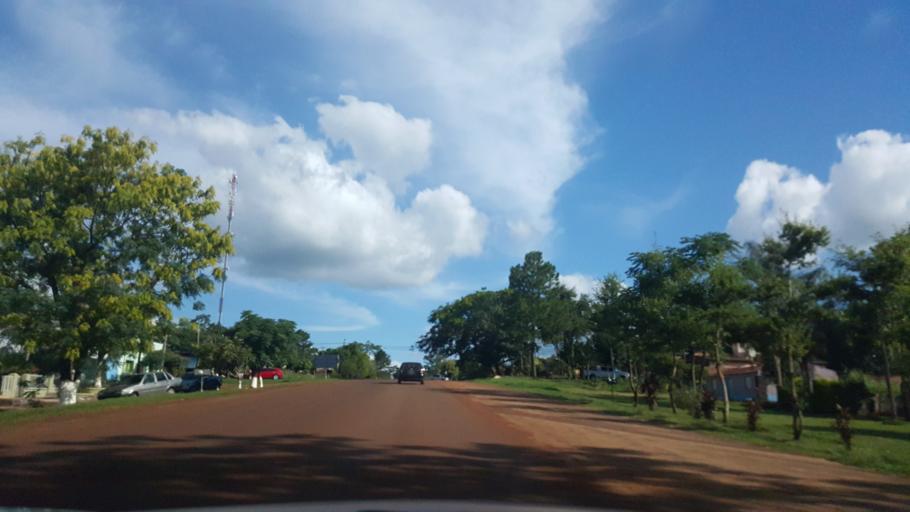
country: AR
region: Misiones
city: Santa Ana
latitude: -27.3646
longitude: -55.5852
